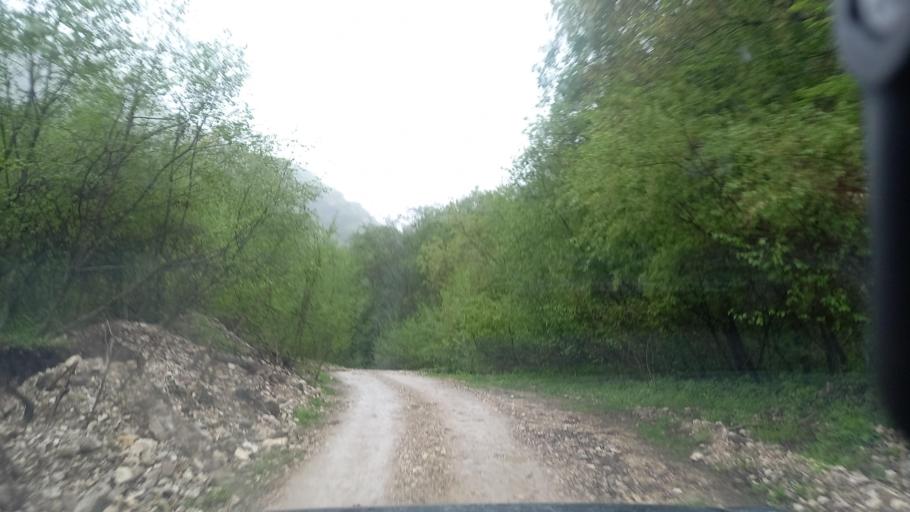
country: RU
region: Kabardino-Balkariya
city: Gundelen
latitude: 43.5823
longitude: 43.1143
